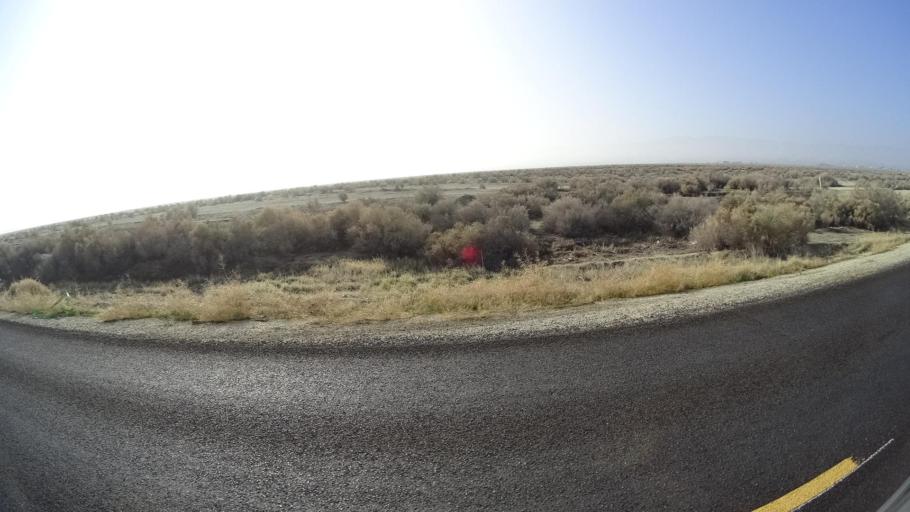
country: US
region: California
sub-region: Kern County
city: Ford City
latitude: 35.1805
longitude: -119.4991
